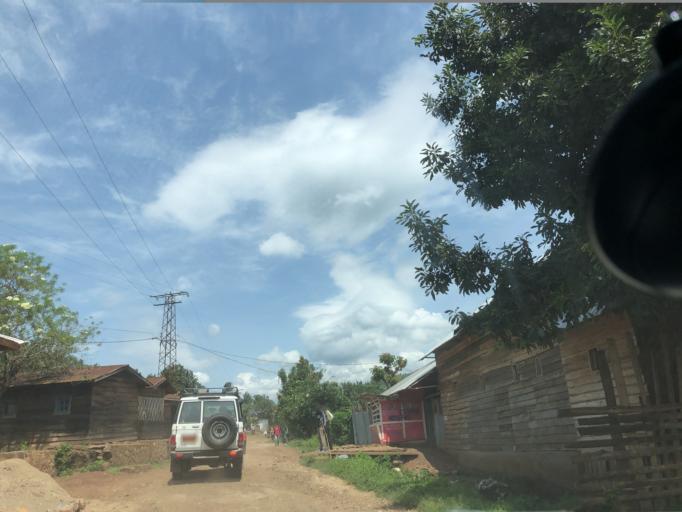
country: CD
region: Nord Kivu
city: Sake
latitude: -1.7082
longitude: 29.0205
